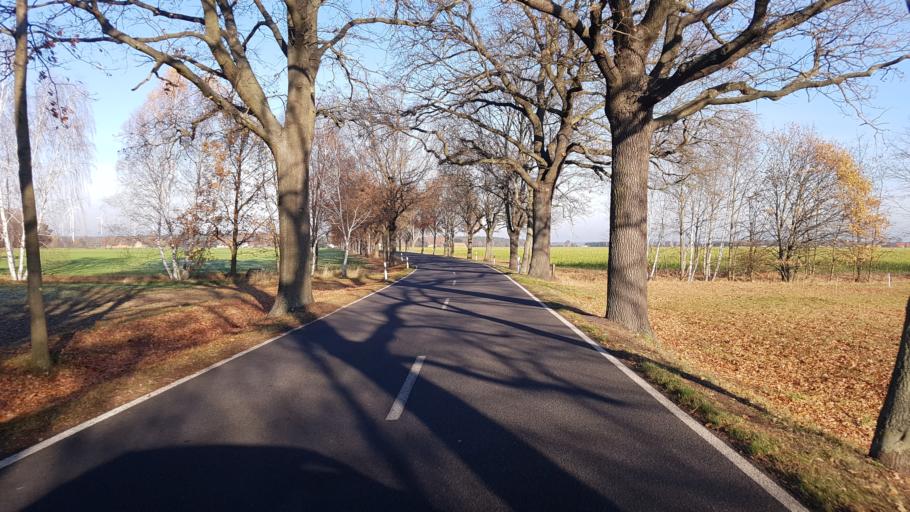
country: DE
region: Brandenburg
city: Sallgast
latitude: 51.5997
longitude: 13.8459
